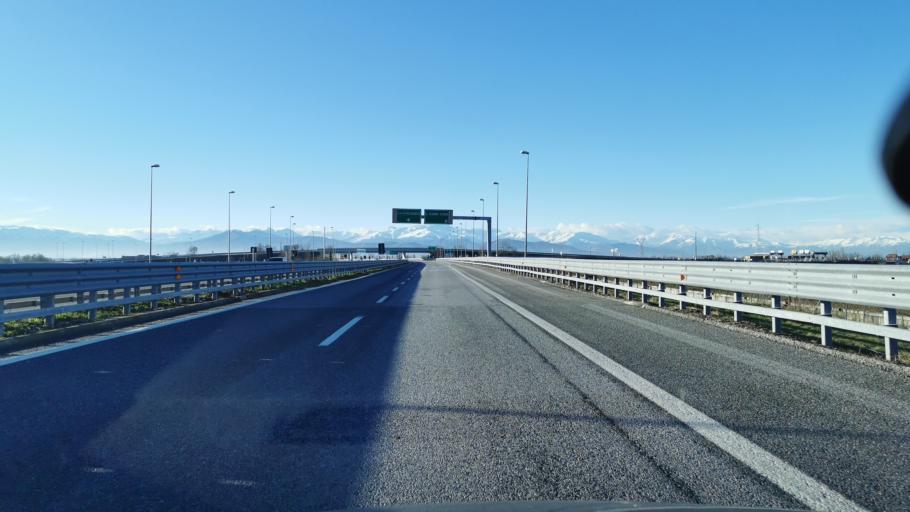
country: IT
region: Piedmont
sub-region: Provincia di Cuneo
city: Montanera
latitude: 44.4751
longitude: 7.6966
